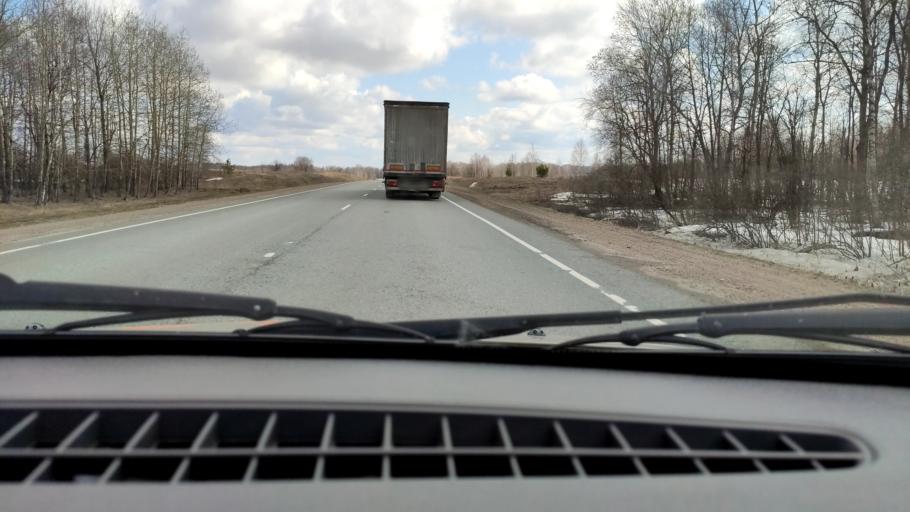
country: RU
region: Bashkortostan
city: Kudeyevskiy
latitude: 54.8170
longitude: 56.7797
